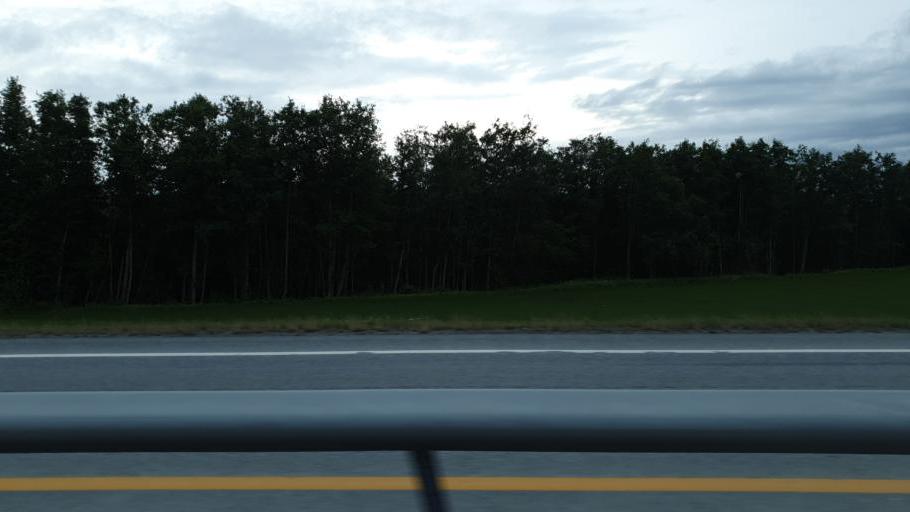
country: NO
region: Sor-Trondelag
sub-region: Melhus
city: Melhus
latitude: 63.2713
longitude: 10.2865
